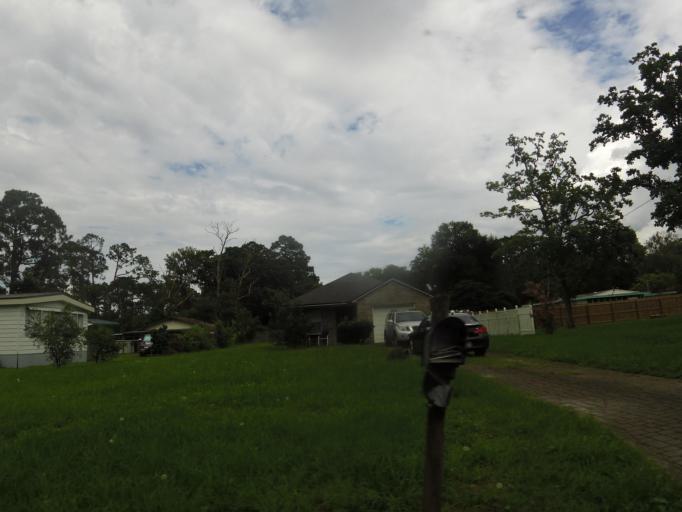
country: US
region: Florida
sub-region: Duval County
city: Jacksonville
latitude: 30.3097
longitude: -81.5360
